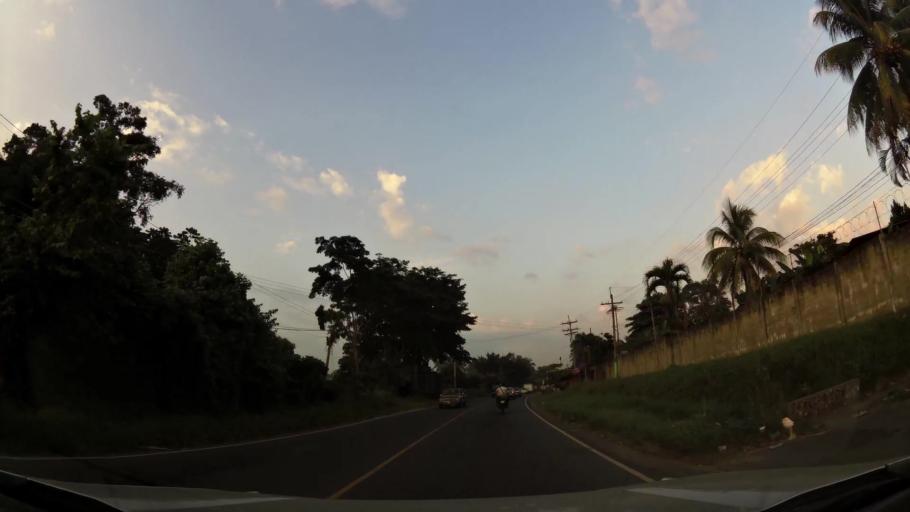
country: GT
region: Retalhuleu
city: San Sebastian
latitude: 14.5709
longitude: -91.6488
